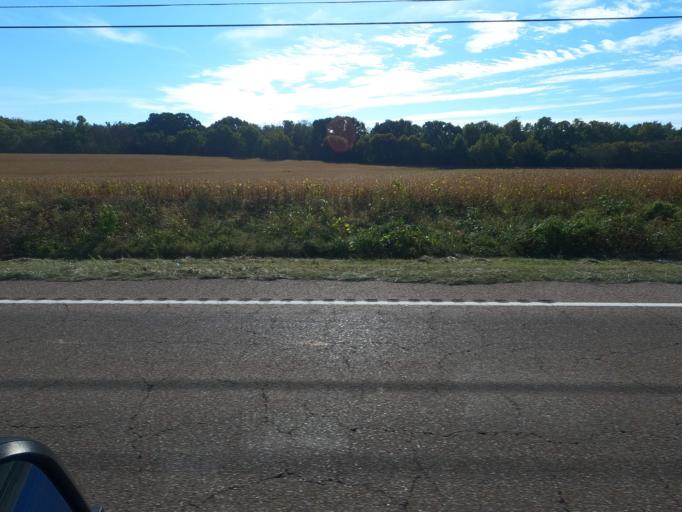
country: US
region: Tennessee
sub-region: Tipton County
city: Covington
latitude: 35.5273
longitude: -89.6869
